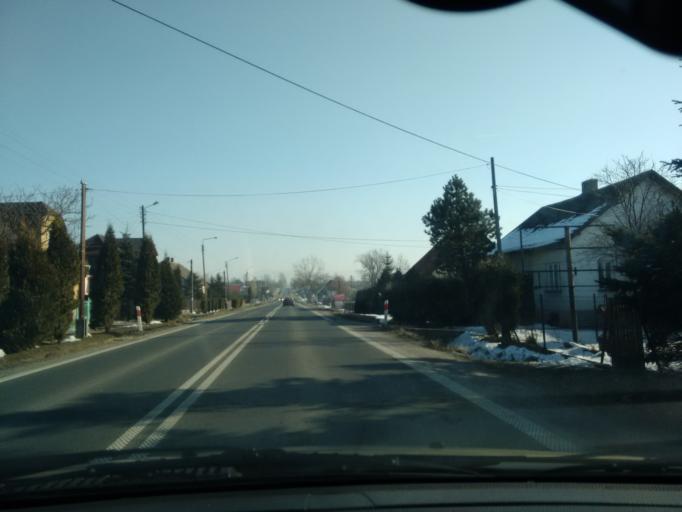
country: PL
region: Lesser Poland Voivodeship
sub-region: Powiat oswiecimski
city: Bulowice
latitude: 49.8693
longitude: 19.3051
